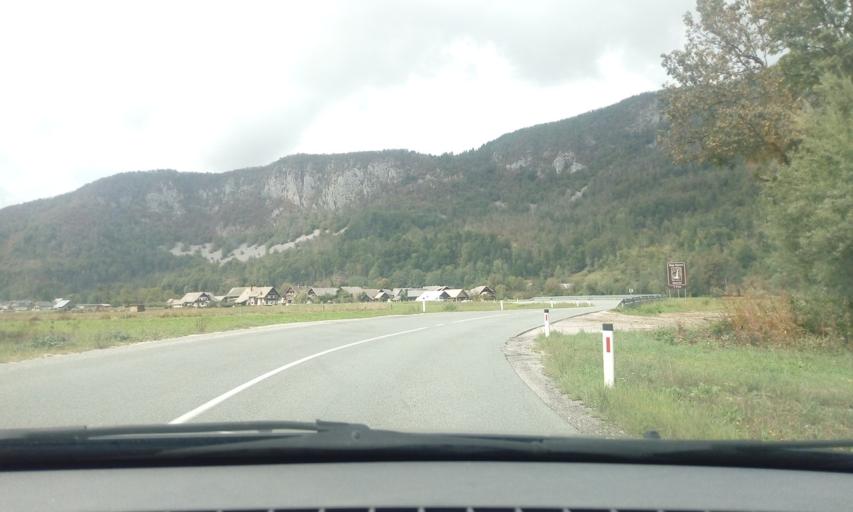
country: SI
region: Bohinj
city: Bohinjska Bistrica
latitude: 46.2722
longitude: 13.9292
